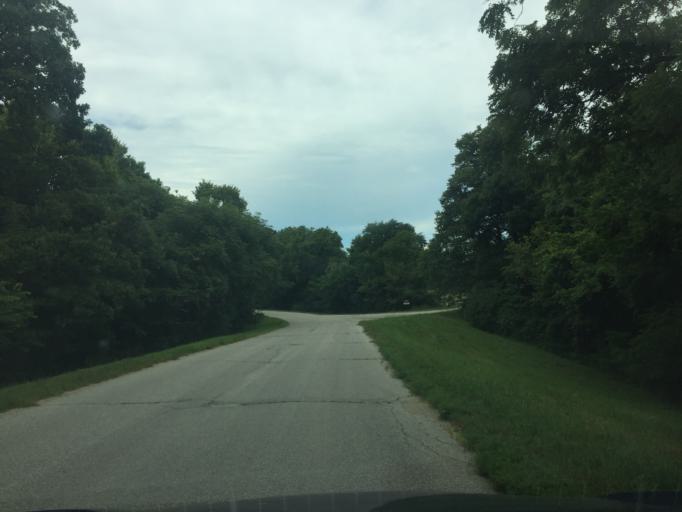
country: US
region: Missouri
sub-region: Platte County
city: Weston
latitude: 39.3708
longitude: -94.9255
